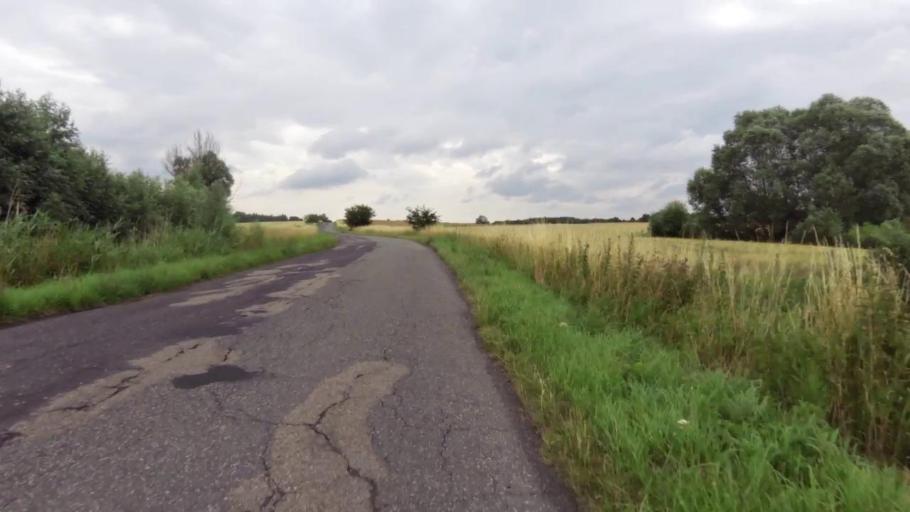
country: PL
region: West Pomeranian Voivodeship
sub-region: Powiat mysliborski
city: Mysliborz
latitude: 52.9543
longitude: 14.8802
